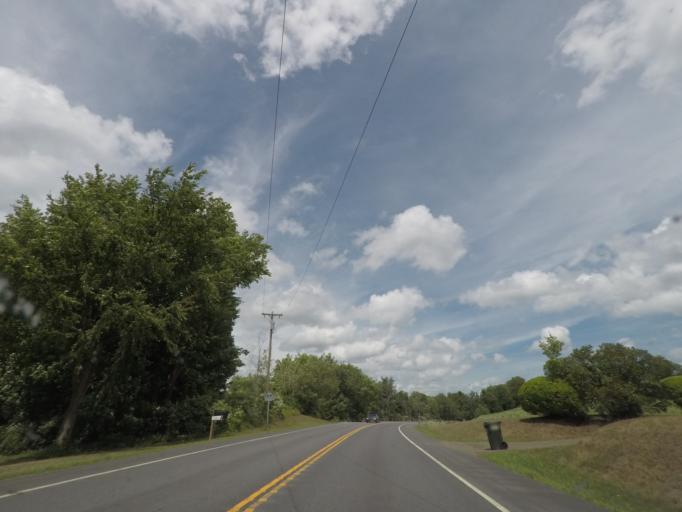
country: US
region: New York
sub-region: Rensselaer County
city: Poestenkill
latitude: 42.6774
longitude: -73.5692
